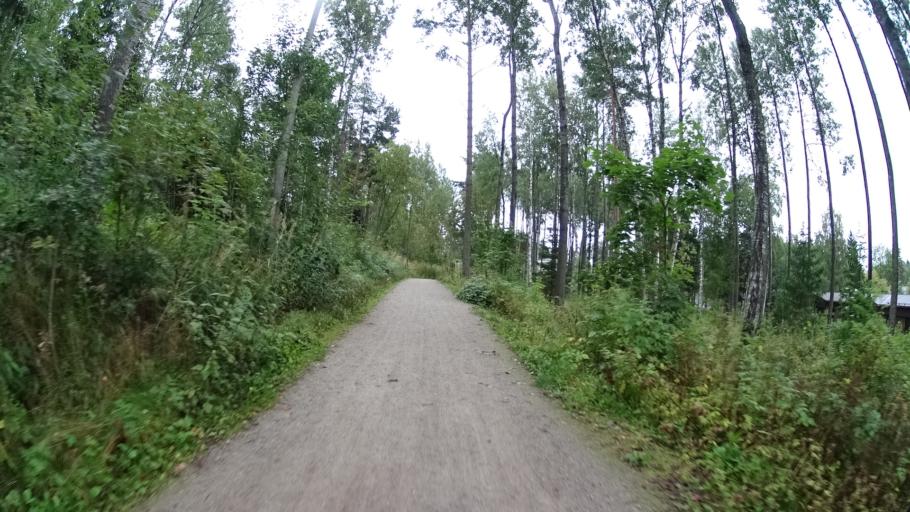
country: FI
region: Uusimaa
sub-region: Helsinki
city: Espoo
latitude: 60.1798
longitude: 24.6483
